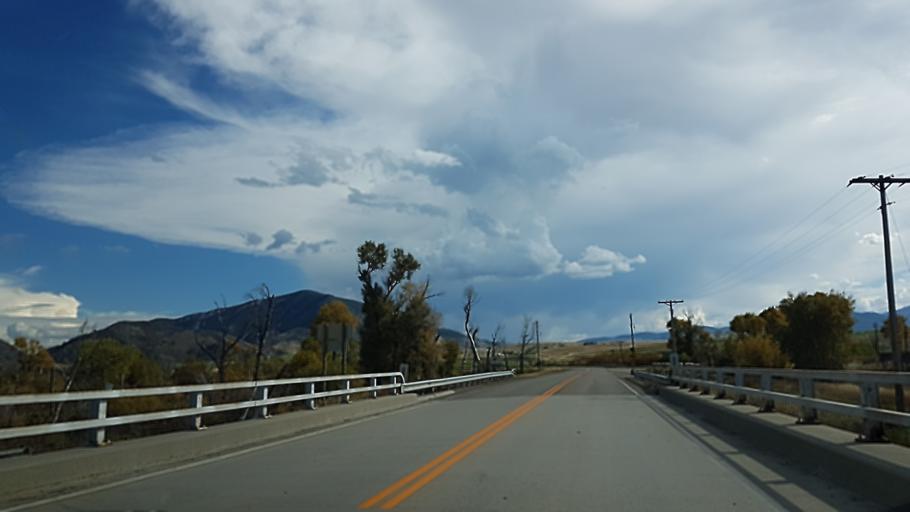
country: US
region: Montana
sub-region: Jefferson County
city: Whitehall
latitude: 45.8548
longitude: -111.9508
